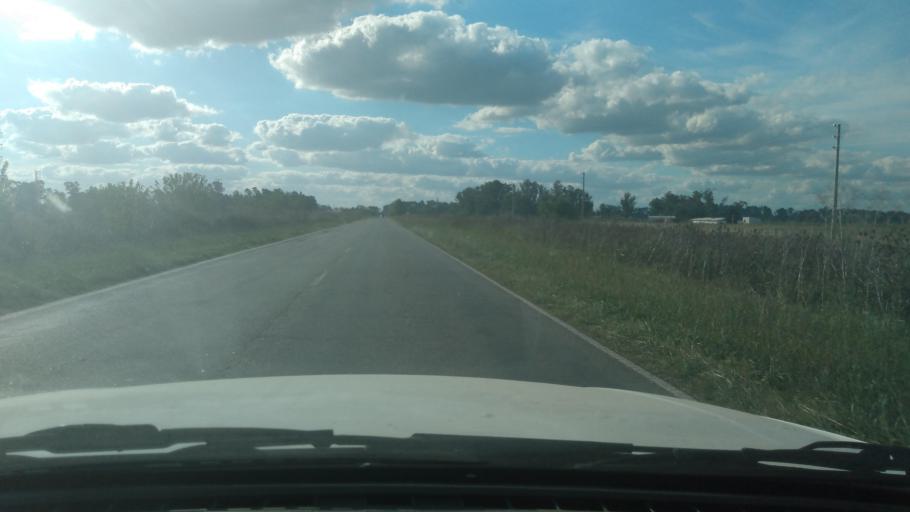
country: AR
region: Buenos Aires
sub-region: Partido de Mercedes
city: Mercedes
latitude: -34.7264
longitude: -59.3920
